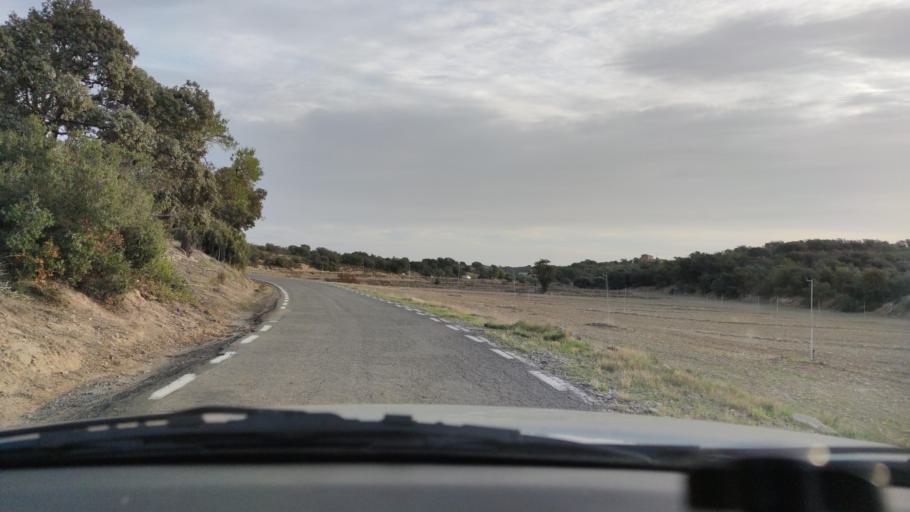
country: ES
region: Catalonia
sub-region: Provincia de Lleida
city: Agramunt
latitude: 41.8352
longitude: 1.0713
